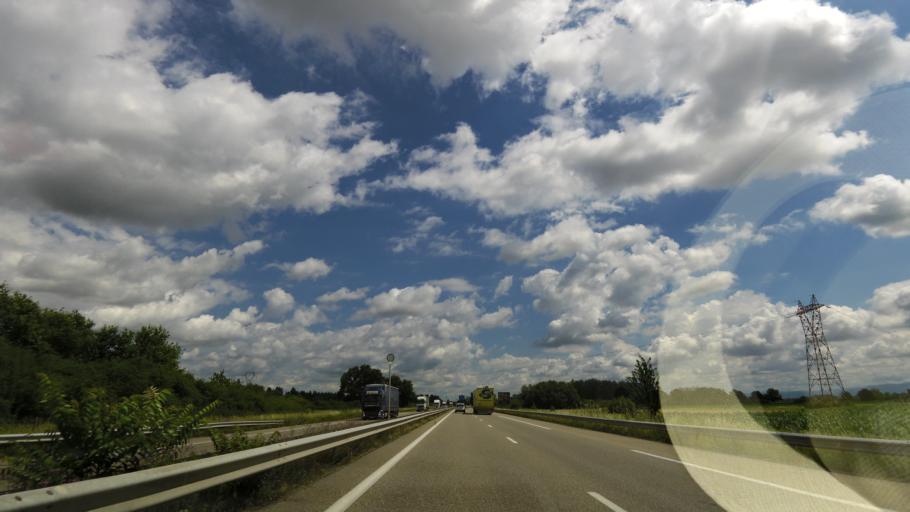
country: FR
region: Alsace
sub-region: Departement du Bas-Rhin
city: Gambsheim
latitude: 48.7149
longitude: 7.8708
